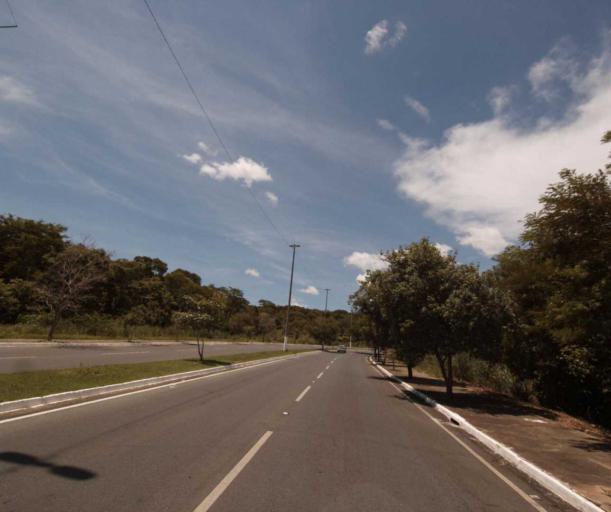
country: BR
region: Mato Grosso
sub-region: Cuiaba
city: Cuiaba
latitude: -15.5732
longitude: -56.1078
